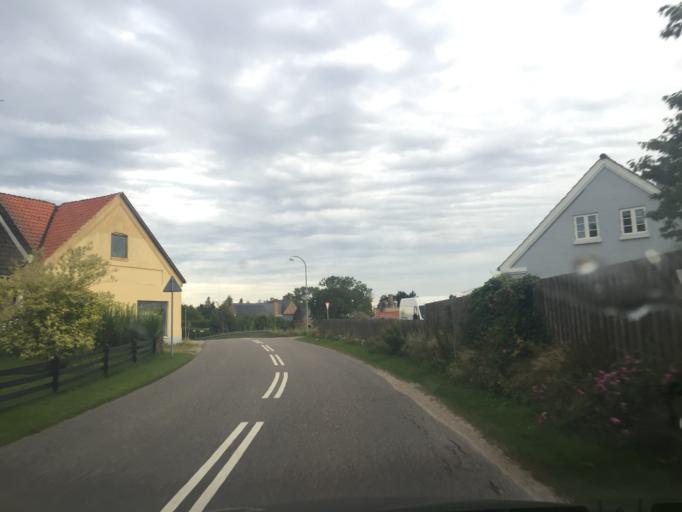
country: DK
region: Capital Region
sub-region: Egedal Kommune
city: Vekso
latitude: 55.7128
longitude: 12.2175
